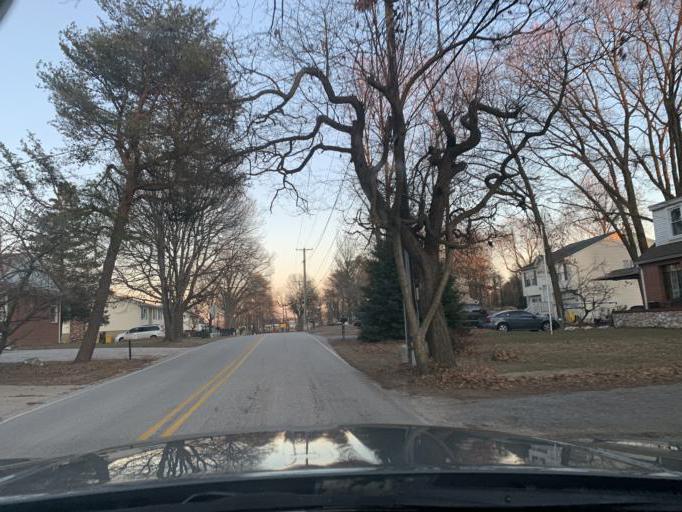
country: US
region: Maryland
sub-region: Anne Arundel County
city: Glen Burnie
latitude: 39.1543
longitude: -76.6394
